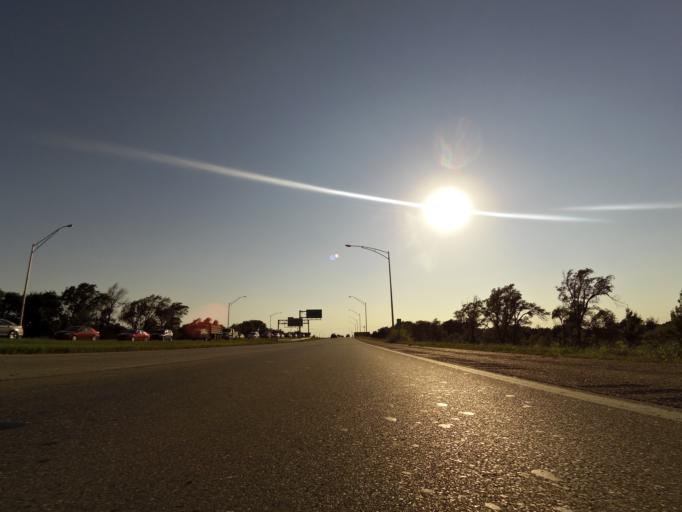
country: US
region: Kansas
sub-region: Sedgwick County
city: Park City
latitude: 37.7586
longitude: -97.3320
